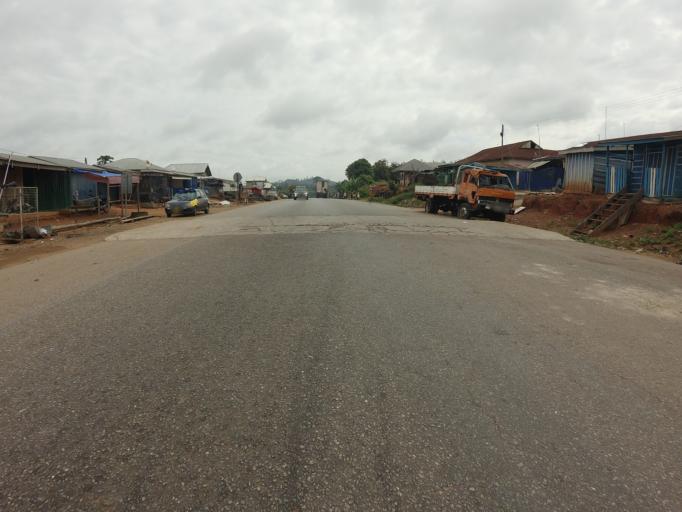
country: GH
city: Bechem
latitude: 7.1359
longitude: -1.7351
